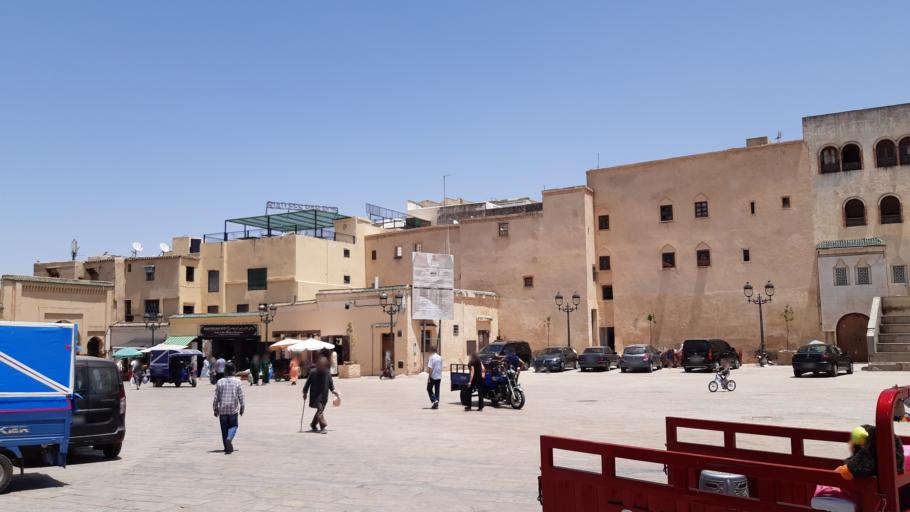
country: MA
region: Fes-Boulemane
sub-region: Fes
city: Fes
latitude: 34.0626
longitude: -4.9727
